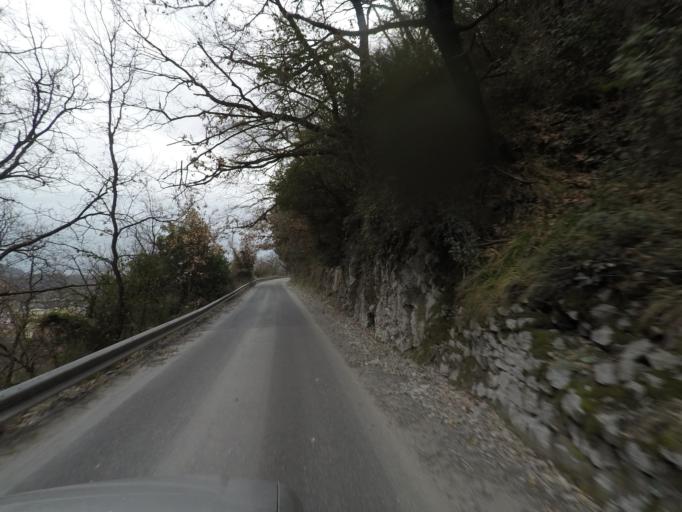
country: IT
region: Tuscany
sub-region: Provincia di Massa-Carrara
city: Carrara
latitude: 44.0848
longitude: 10.1097
